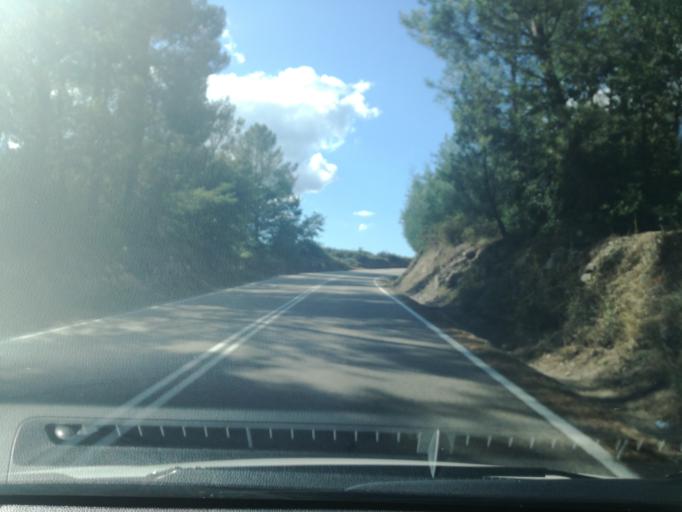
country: ES
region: Galicia
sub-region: Provincia de Ourense
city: Lobios
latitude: 41.8790
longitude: -8.0983
